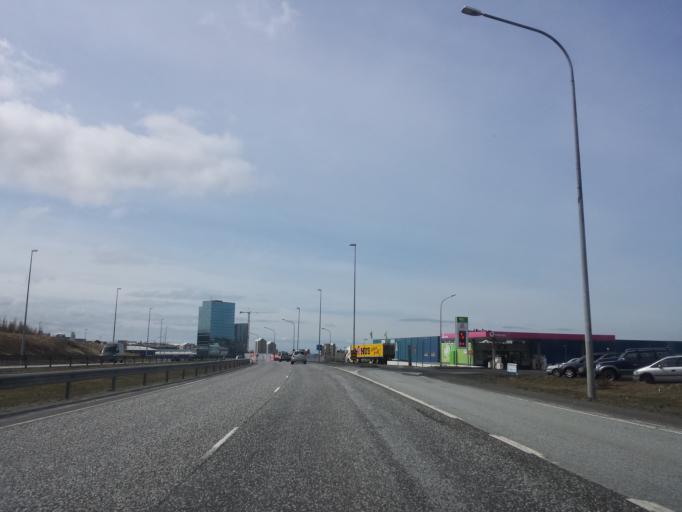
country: IS
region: Capital Region
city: Reykjavik
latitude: 64.1051
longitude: -21.8651
